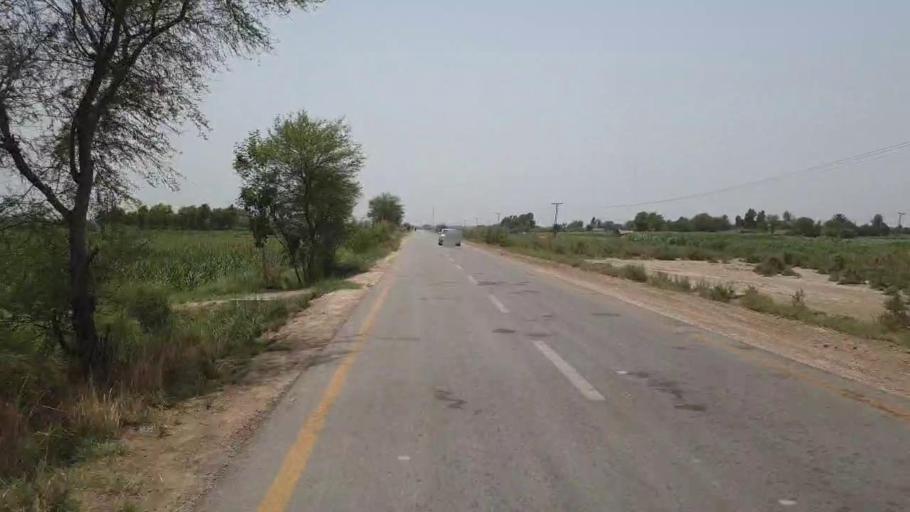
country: PK
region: Sindh
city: Moro
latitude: 26.6006
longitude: 68.0816
